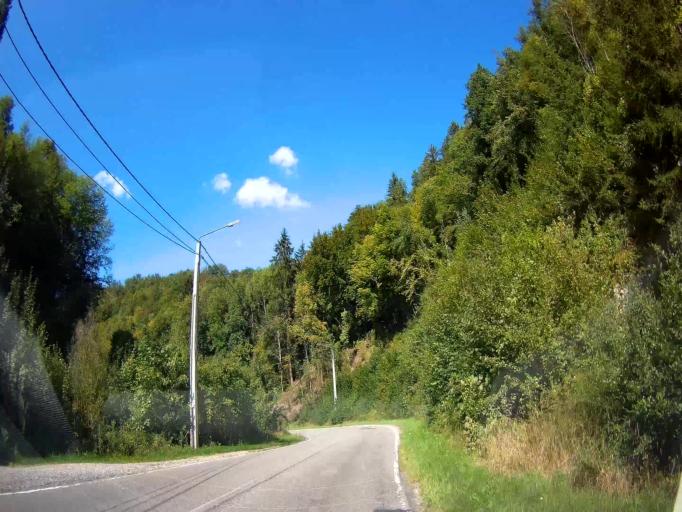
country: BE
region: Wallonia
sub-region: Province de Namur
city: Hastiere-Lavaux
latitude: 50.2229
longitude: 4.8158
